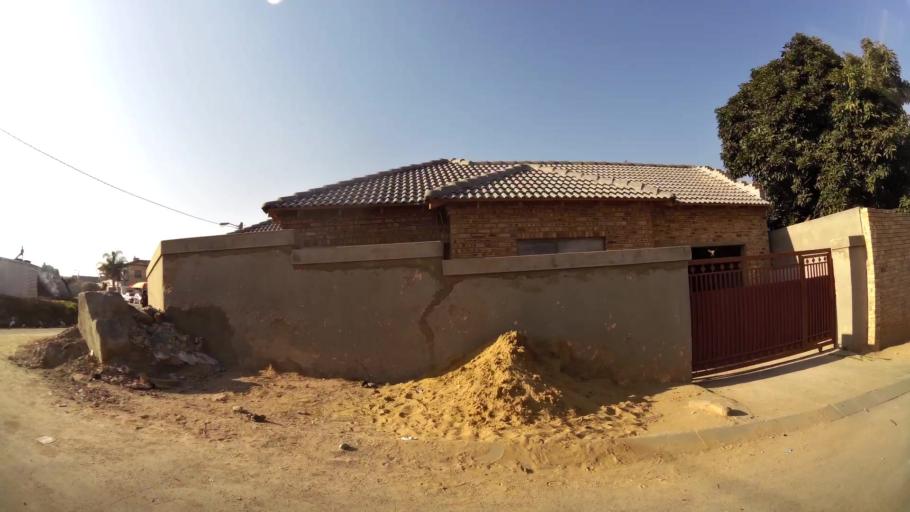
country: ZA
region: Gauteng
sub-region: City of Johannesburg Metropolitan Municipality
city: Modderfontein
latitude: -26.0997
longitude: 28.1143
